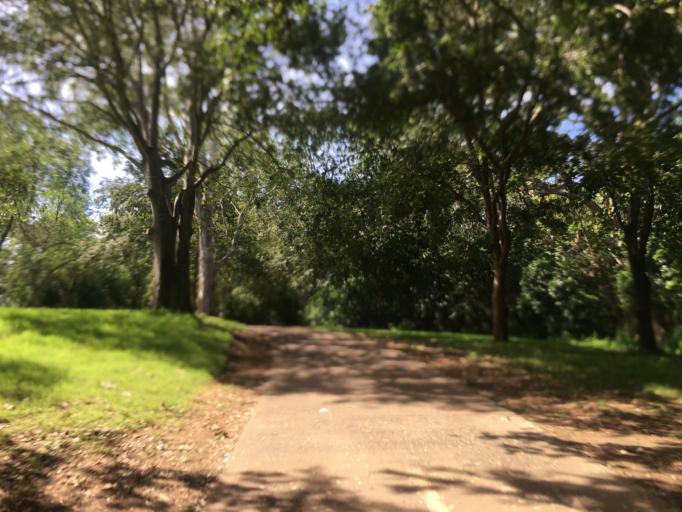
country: AU
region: New South Wales
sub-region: Camden
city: Elderslie
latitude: -34.0628
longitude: 150.6998
